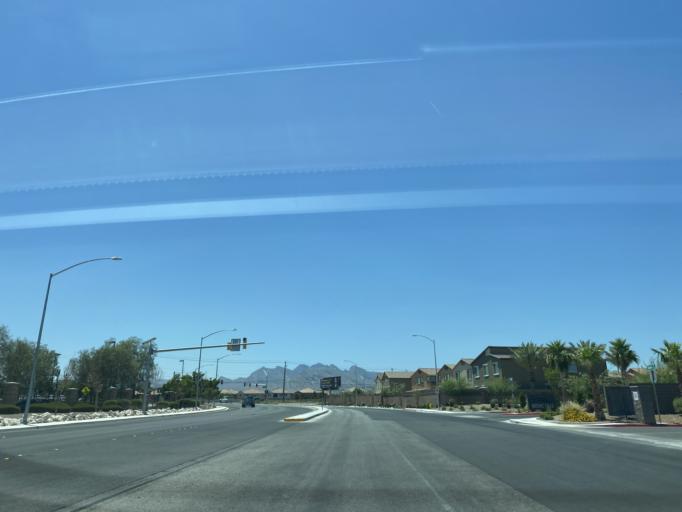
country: US
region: Nevada
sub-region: Clark County
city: Las Vegas
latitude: 36.2317
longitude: -115.2227
